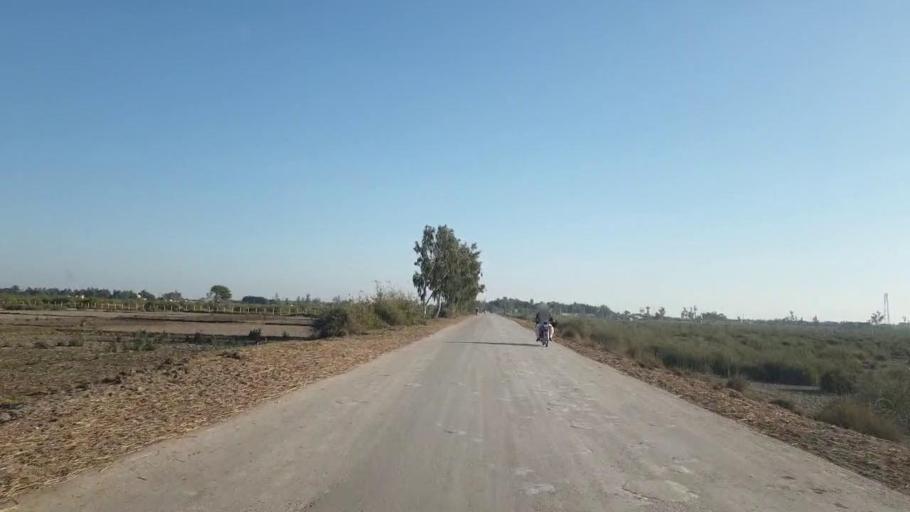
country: PK
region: Sindh
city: Dokri
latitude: 27.3364
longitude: 68.1278
